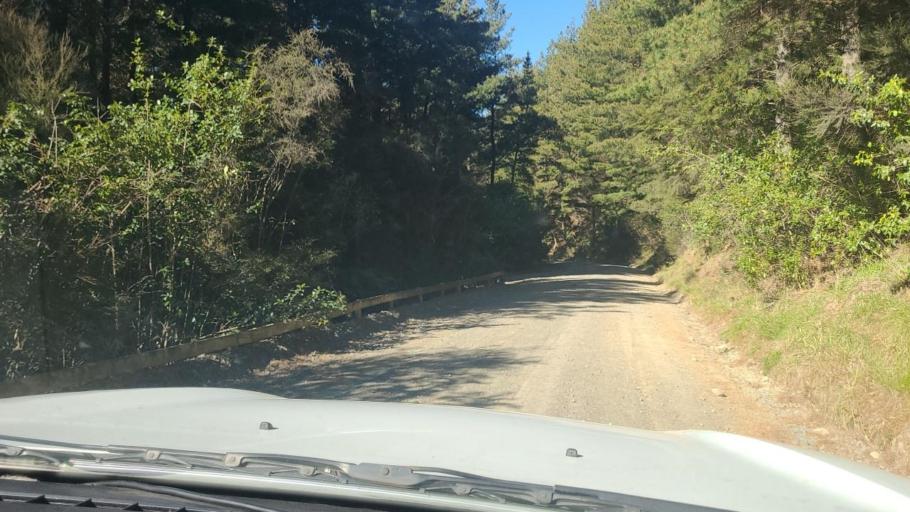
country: NZ
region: Hawke's Bay
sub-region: Napier City
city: Taradale
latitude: -39.4079
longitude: 176.4840
